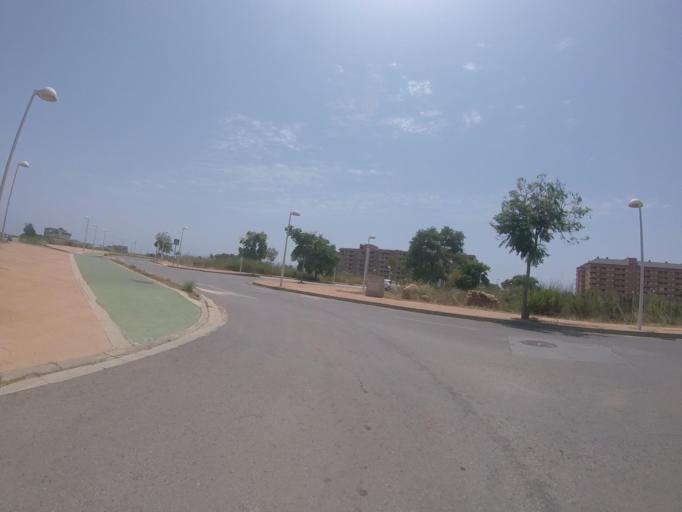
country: ES
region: Valencia
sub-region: Provincia de Castello
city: Orpesa/Oropesa del Mar
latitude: 40.1384
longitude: 0.1621
